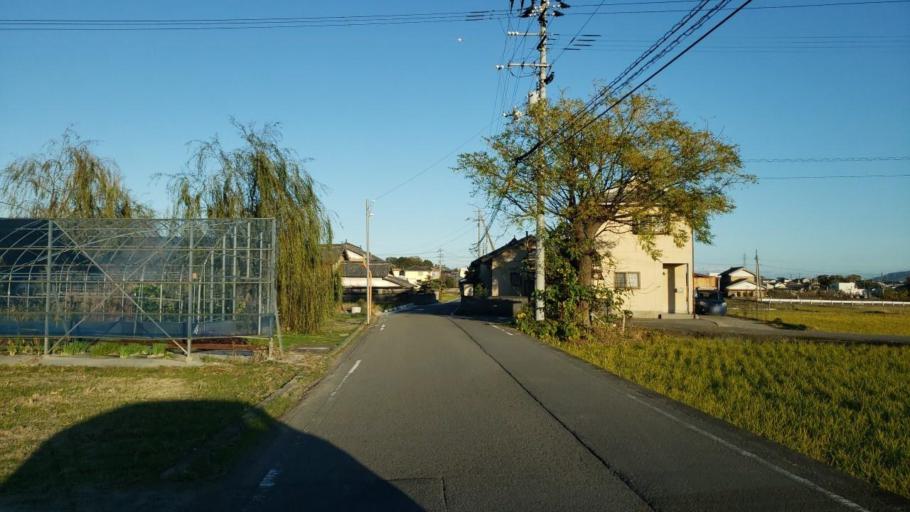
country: JP
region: Tokushima
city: Kamojimacho-jogejima
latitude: 34.0913
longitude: 134.2766
